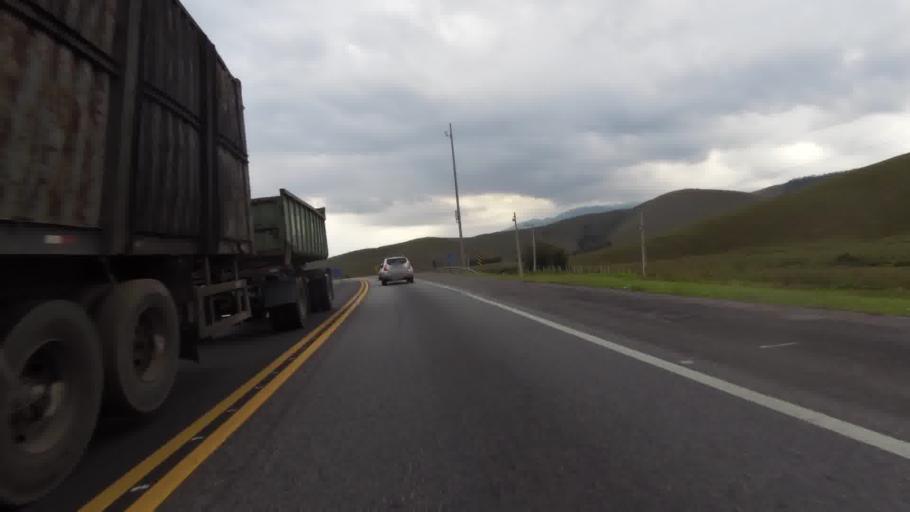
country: BR
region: Rio de Janeiro
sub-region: Rio Bonito
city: Rio Bonito
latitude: -22.6820
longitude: -42.5335
